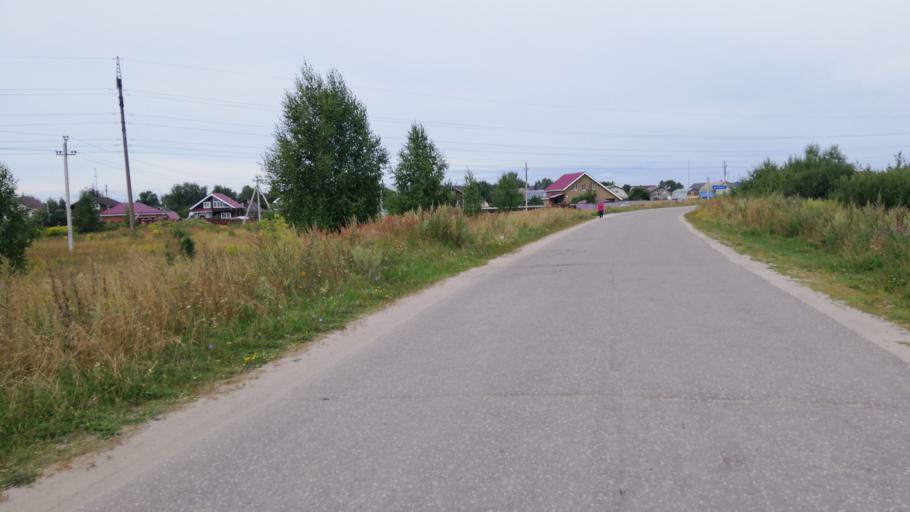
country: RU
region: Nizjnij Novgorod
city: Gorodets
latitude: 56.6630
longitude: 43.4919
